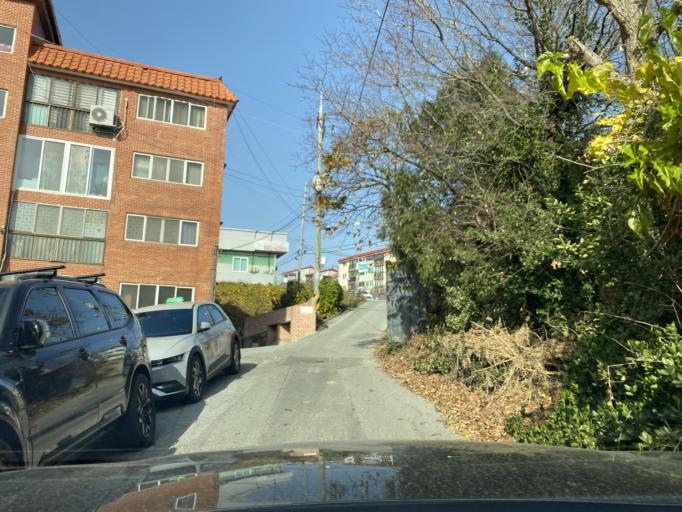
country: KR
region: Chungcheongnam-do
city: Yesan
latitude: 36.6853
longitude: 126.8455
